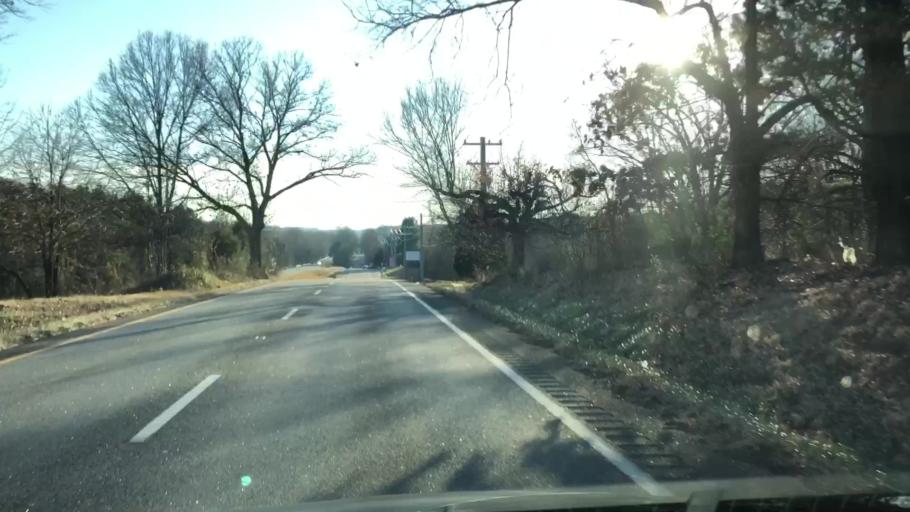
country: US
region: Virginia
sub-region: Albemarle County
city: Hollymead
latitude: 38.1737
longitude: -78.4087
